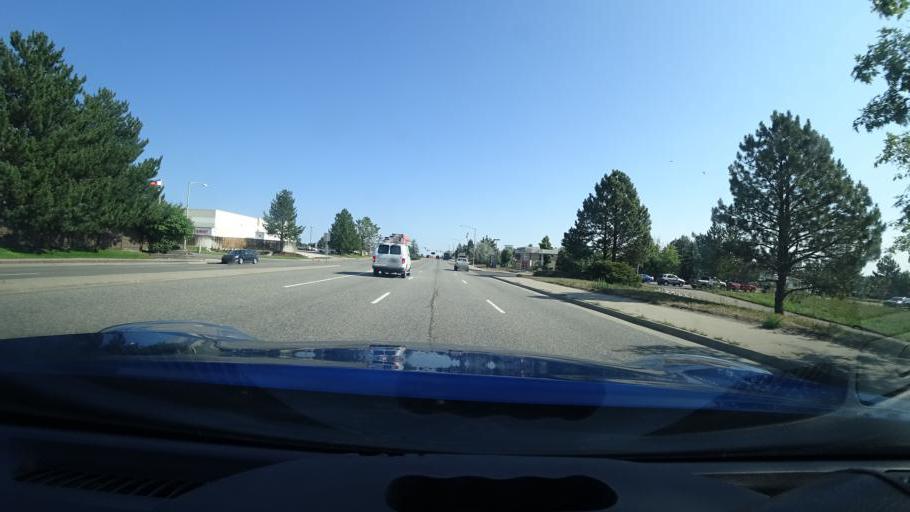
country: US
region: Colorado
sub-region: Adams County
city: Aurora
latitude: 39.6940
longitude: -104.8098
